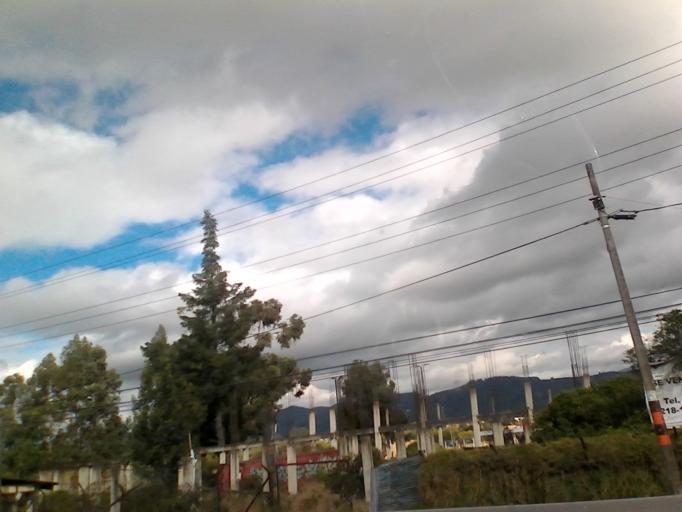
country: CO
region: Cundinamarca
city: Chia
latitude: 4.8690
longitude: -74.0233
